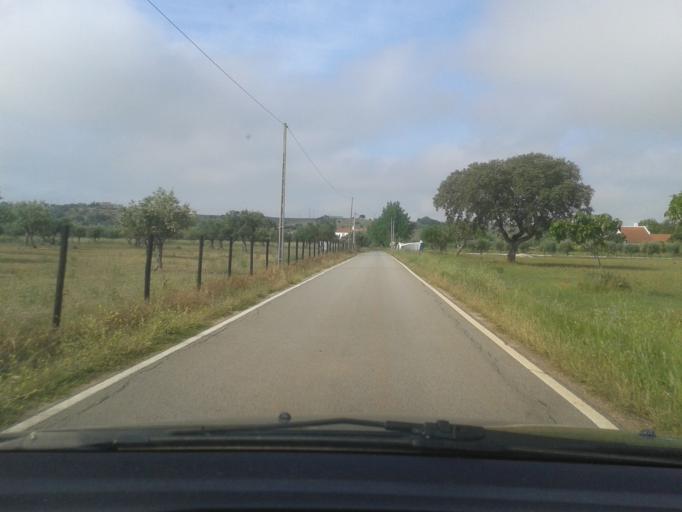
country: PT
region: Portalegre
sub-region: Avis
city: Avis
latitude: 39.0301
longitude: -7.9257
